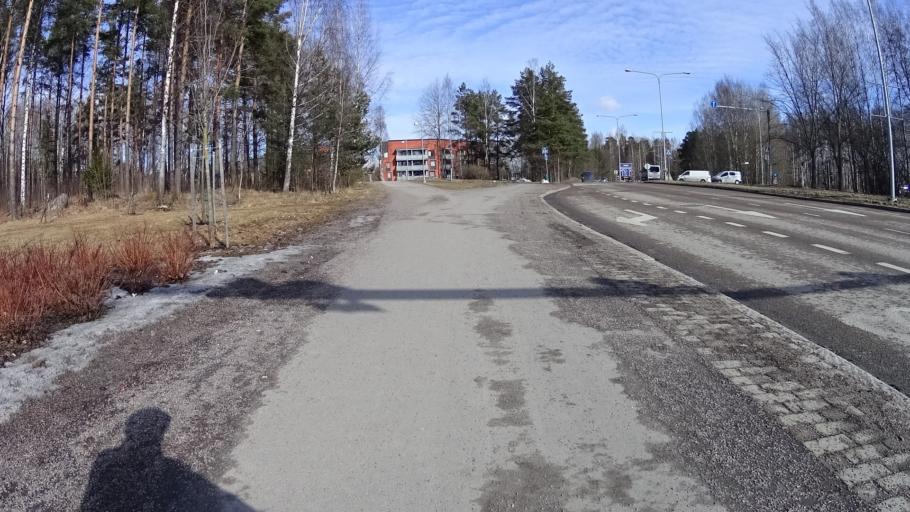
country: FI
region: Uusimaa
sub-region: Helsinki
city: Teekkarikylae
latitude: 60.2455
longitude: 24.8487
